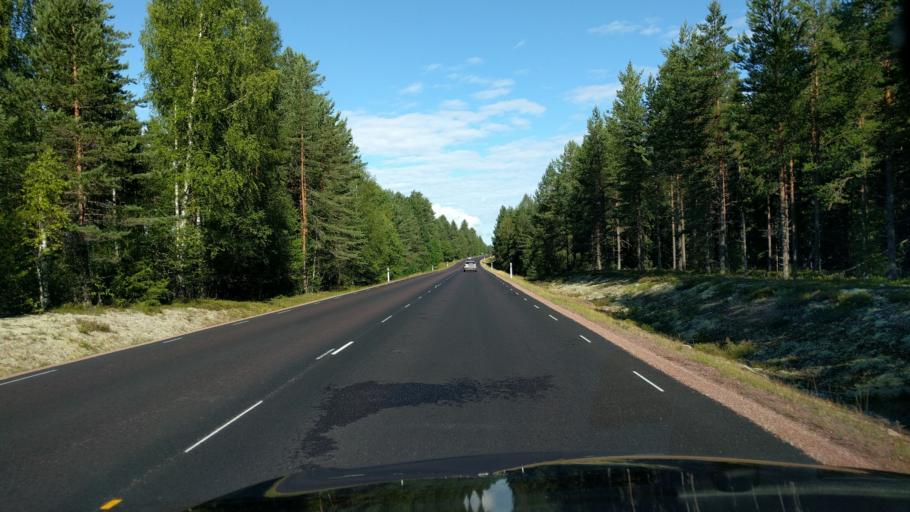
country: SE
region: Dalarna
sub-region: Alvdalens Kommun
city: AElvdalen
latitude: 61.1287
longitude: 14.1866
